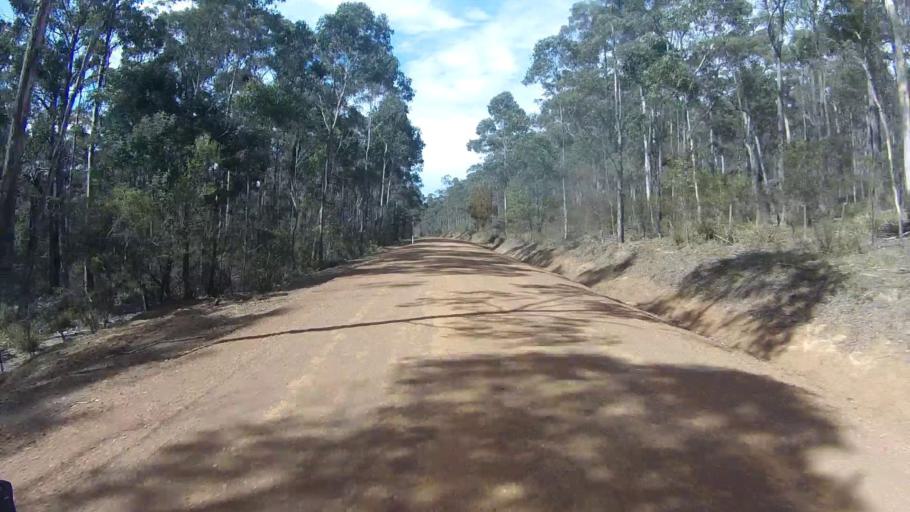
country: AU
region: Tasmania
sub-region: Sorell
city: Sorell
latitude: -42.6233
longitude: 147.9031
